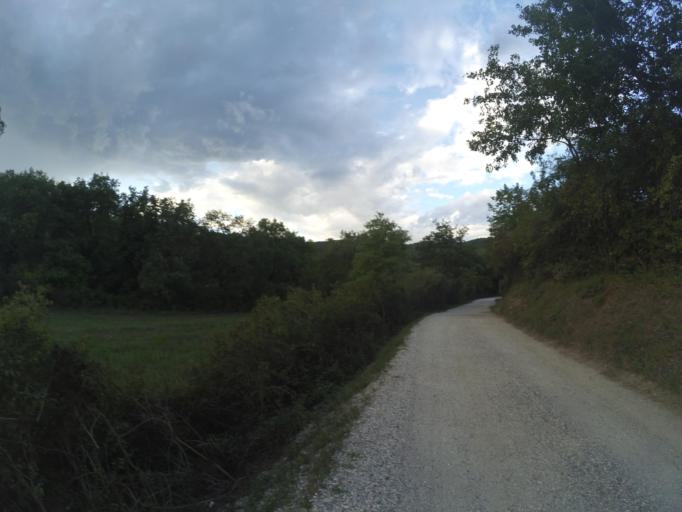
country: IT
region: Tuscany
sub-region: Province of Arezzo
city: Castiglion Fibocchi
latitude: 43.5380
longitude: 11.7671
